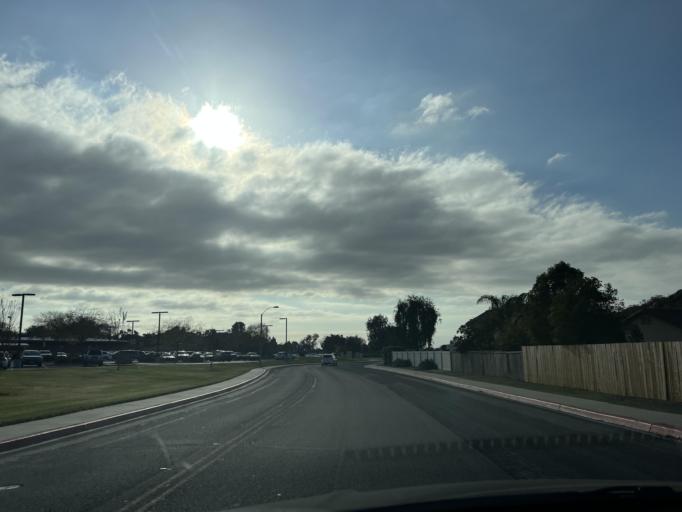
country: US
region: California
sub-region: San Diego County
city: Fairbanks Ranch
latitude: 32.9704
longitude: -117.1250
